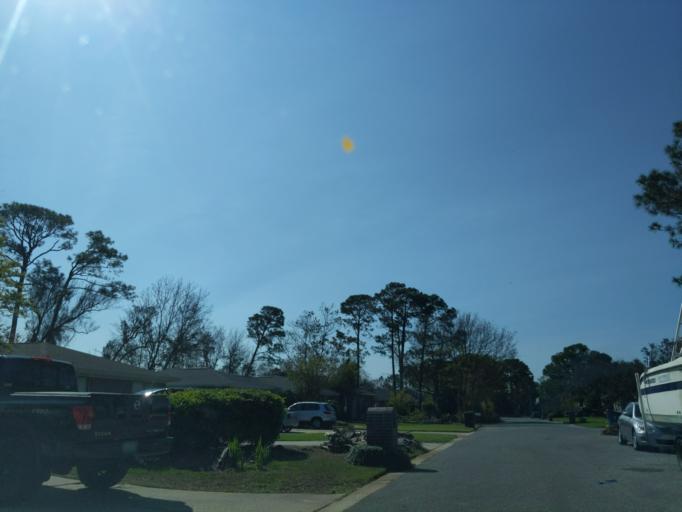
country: US
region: Florida
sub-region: Santa Rosa County
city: Gulf Breeze
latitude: 30.3509
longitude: -87.1858
